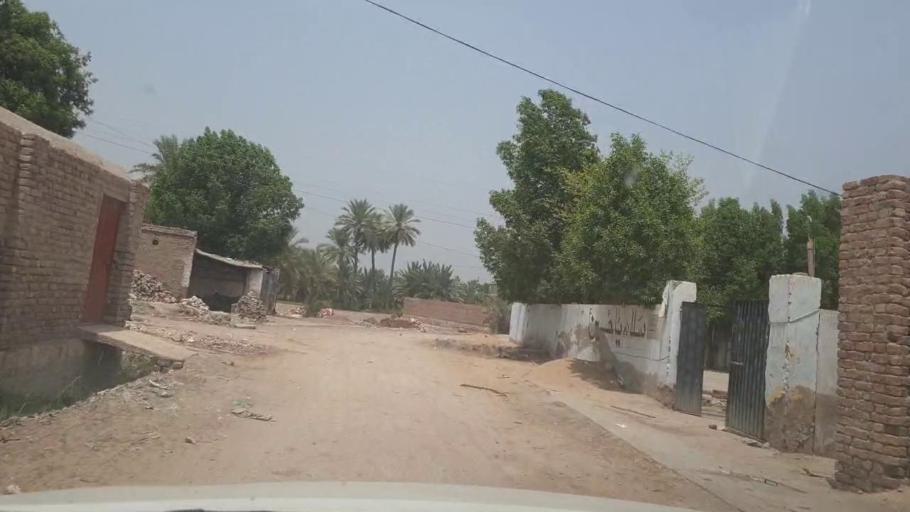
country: PK
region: Sindh
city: Kot Diji
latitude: 27.3674
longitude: 68.7204
